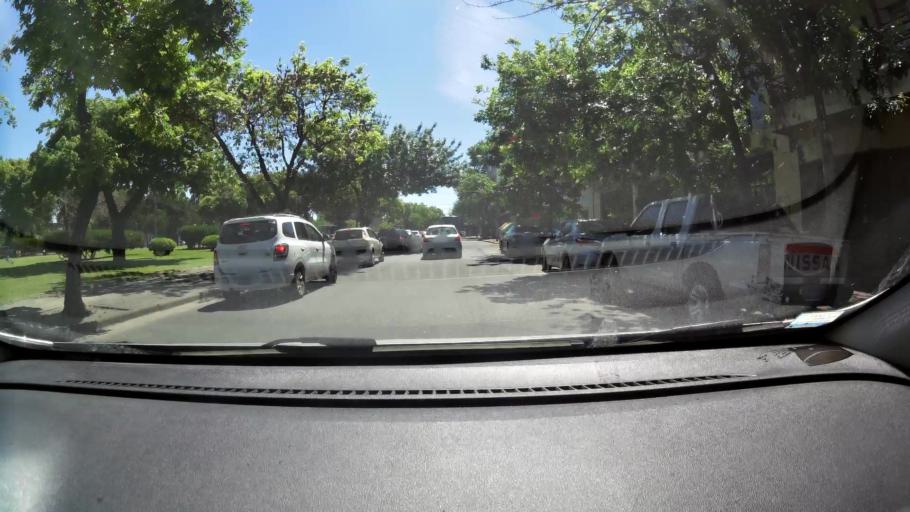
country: AR
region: Santa Fe
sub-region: Departamento de Rosario
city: Rosario
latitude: -32.9385
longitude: -60.6751
